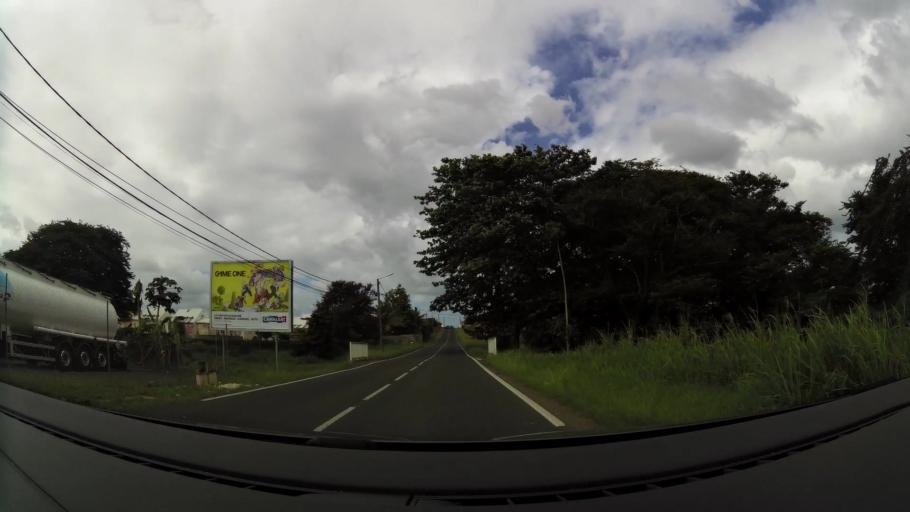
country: GP
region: Guadeloupe
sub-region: Guadeloupe
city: Lamentin
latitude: 16.2615
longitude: -61.6210
